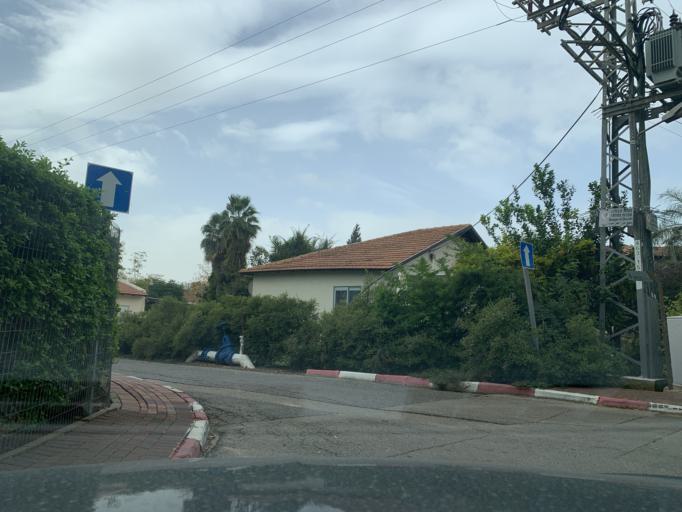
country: IL
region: Central District
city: Jaljulya
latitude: 32.1590
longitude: 34.9450
